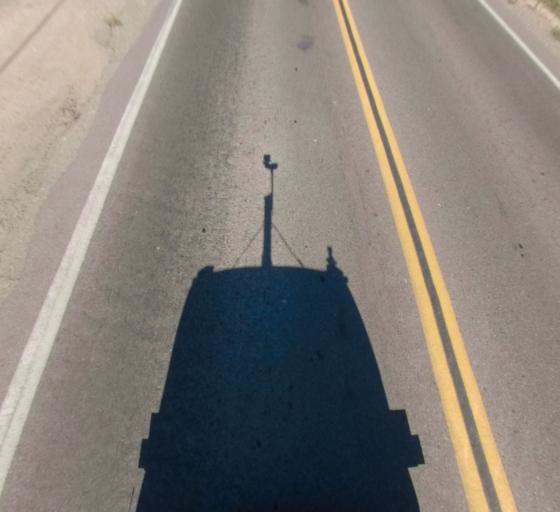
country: US
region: California
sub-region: Fresno County
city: Biola
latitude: 36.8513
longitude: -120.0532
